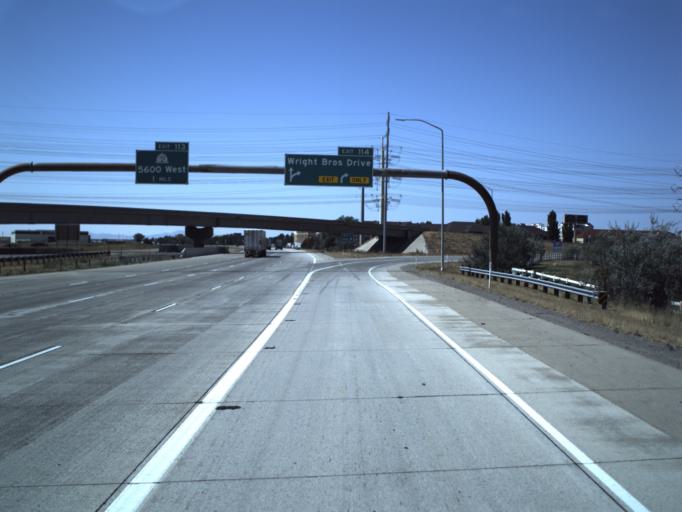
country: US
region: Utah
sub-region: Salt Lake County
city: West Valley City
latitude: 40.7693
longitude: -112.0029
